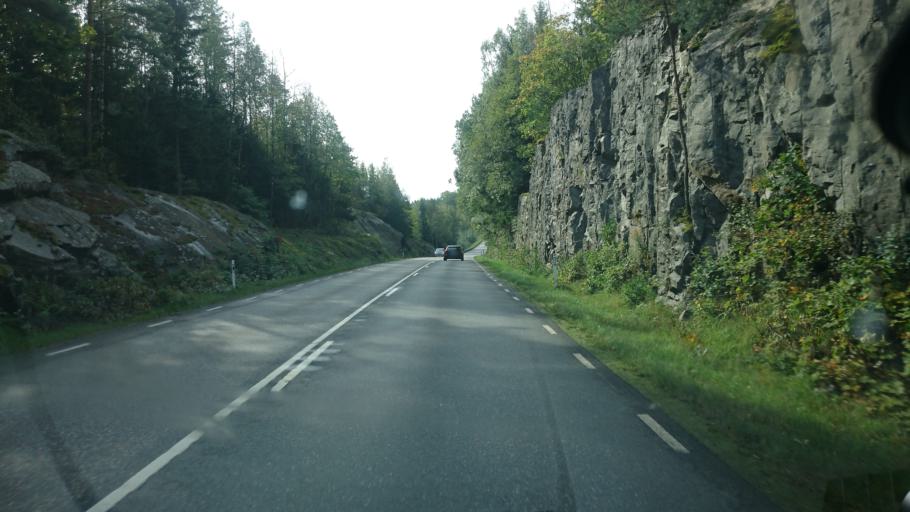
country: SE
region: Vaestra Goetaland
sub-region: Alingsas Kommun
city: Sollebrunn
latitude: 58.0348
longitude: 12.4652
